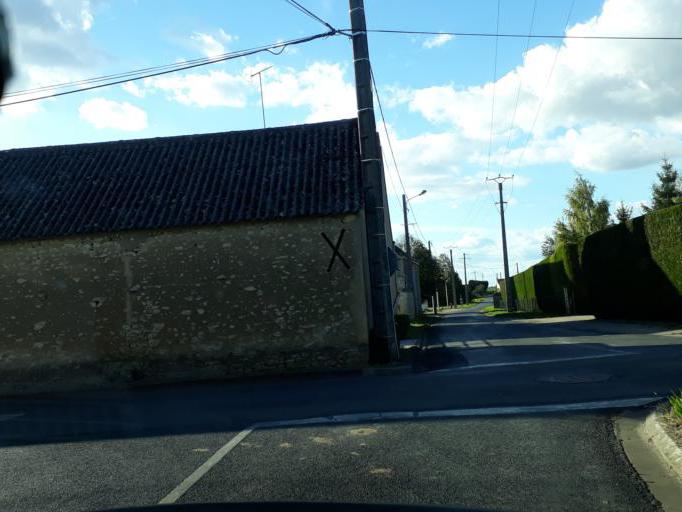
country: FR
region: Centre
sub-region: Departement du Loiret
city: Beaugency
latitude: 47.8300
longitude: 1.5772
